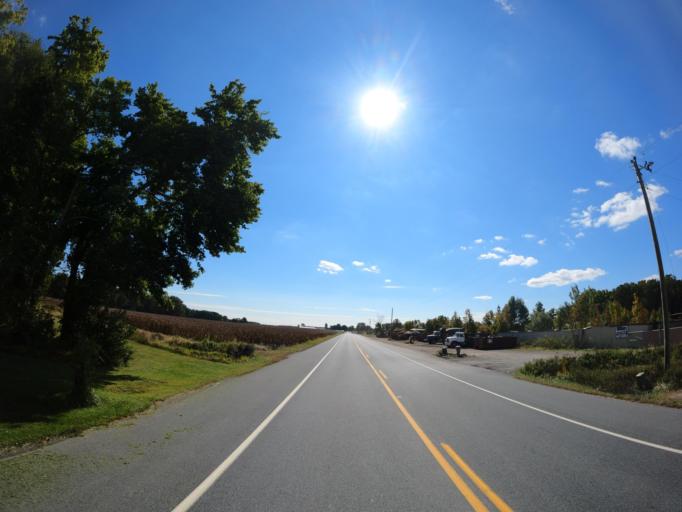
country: US
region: Delaware
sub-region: Sussex County
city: Bridgeville
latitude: 38.8173
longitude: -75.6190
